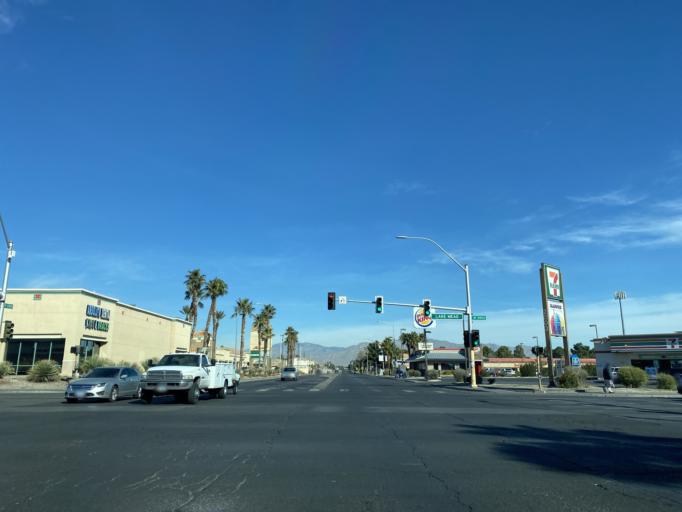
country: US
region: Nevada
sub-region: Clark County
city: Las Vegas
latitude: 36.1956
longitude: -115.2239
